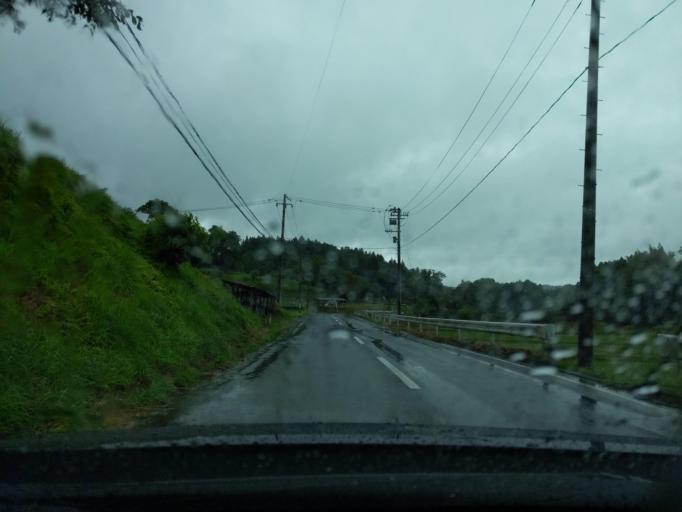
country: JP
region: Fukushima
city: Funehikimachi-funehiki
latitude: 37.4904
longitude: 140.5256
